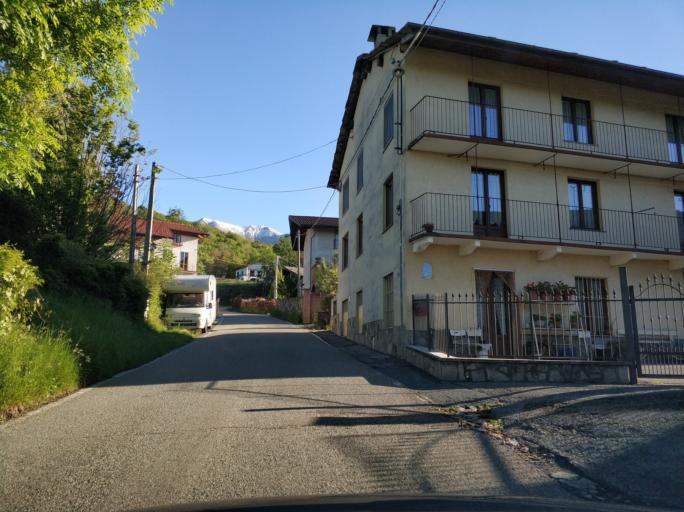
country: IT
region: Piedmont
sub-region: Provincia di Torino
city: Coassolo
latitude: 45.3036
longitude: 7.4672
